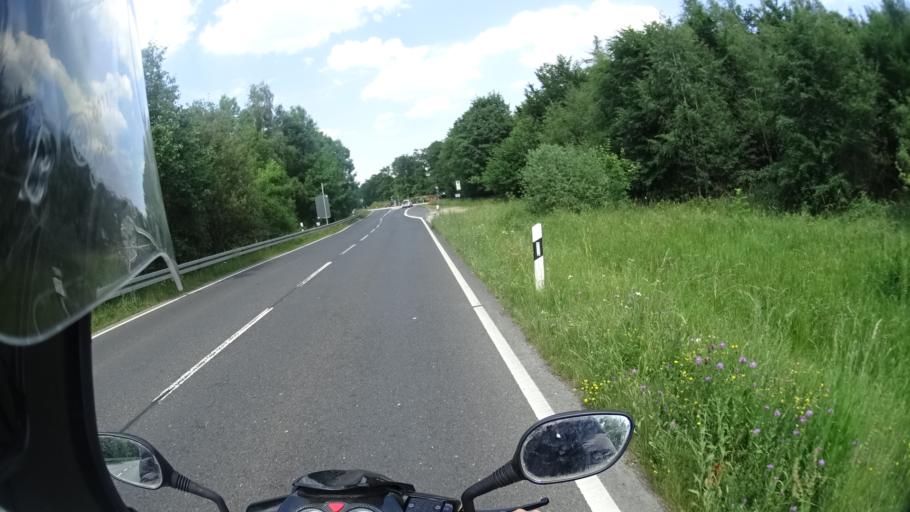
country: DE
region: Hesse
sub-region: Regierungsbezirk Darmstadt
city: Bad Schwalbach
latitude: 50.1219
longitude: 8.0827
